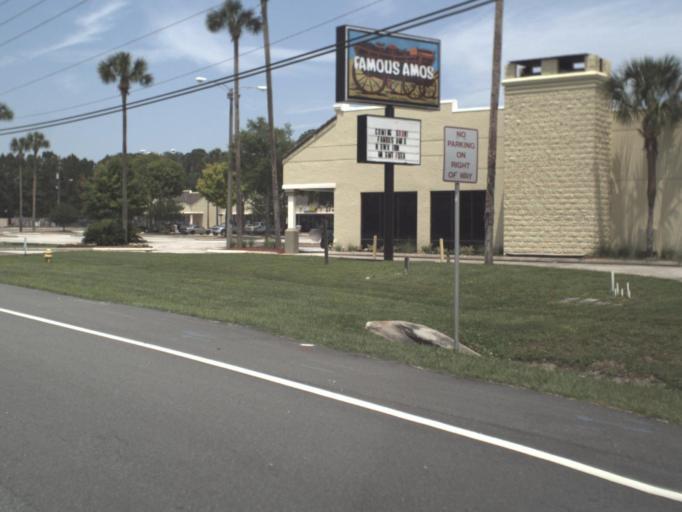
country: US
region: Florida
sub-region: Duval County
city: Jacksonville
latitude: 30.4465
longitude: -81.6395
